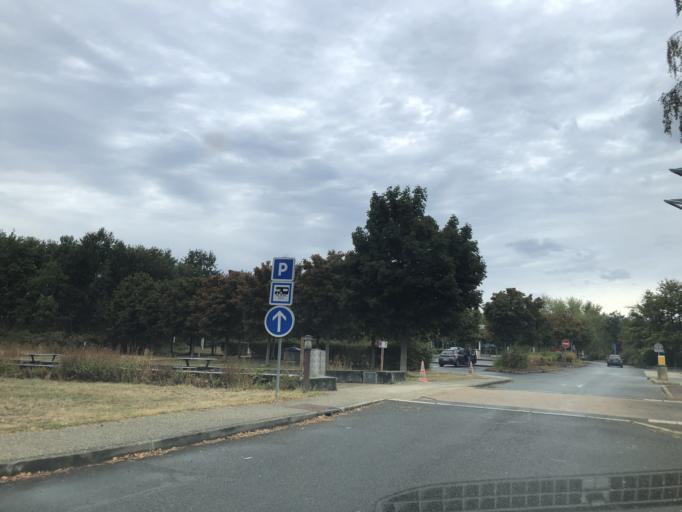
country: FR
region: Ile-de-France
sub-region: Departement de Seine-et-Marne
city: Montereau-Fault-Yonne
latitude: 48.4287
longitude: 2.9321
